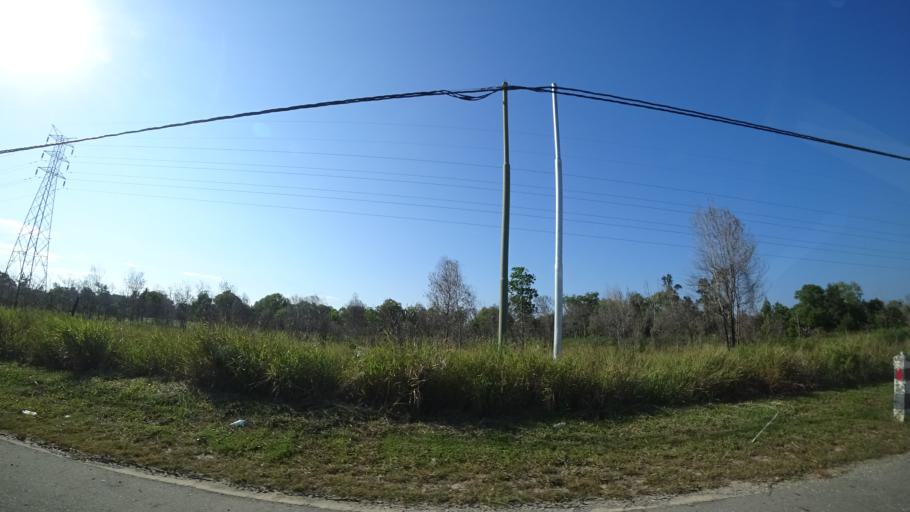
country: BN
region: Tutong
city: Tutong
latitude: 4.7144
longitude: 114.5377
